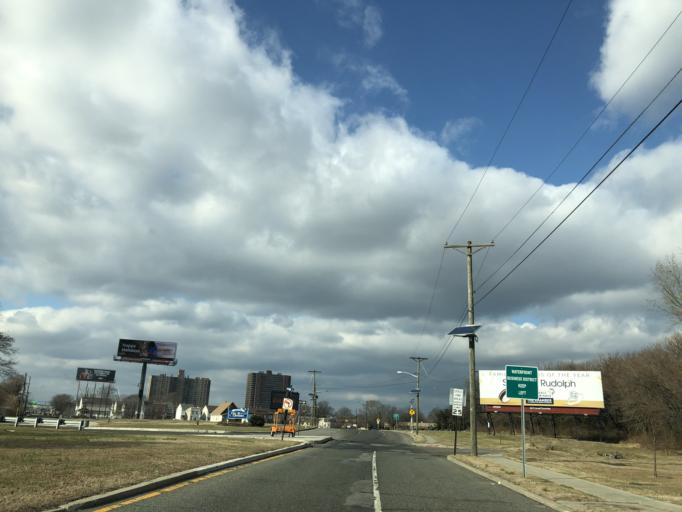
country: US
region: New Jersey
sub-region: Camden County
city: Camden
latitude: 39.9455
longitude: -75.1084
